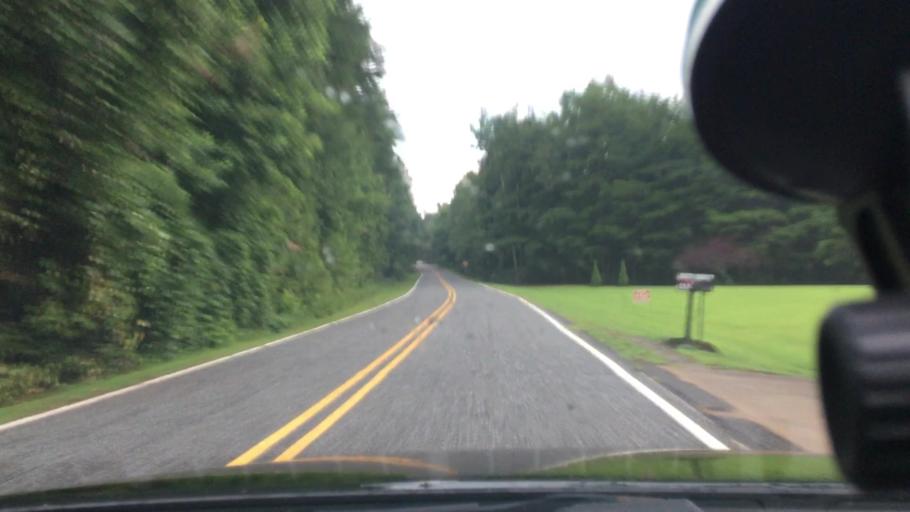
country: US
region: North Carolina
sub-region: Rutherford County
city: Rutherfordton
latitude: 35.3892
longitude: -81.9842
